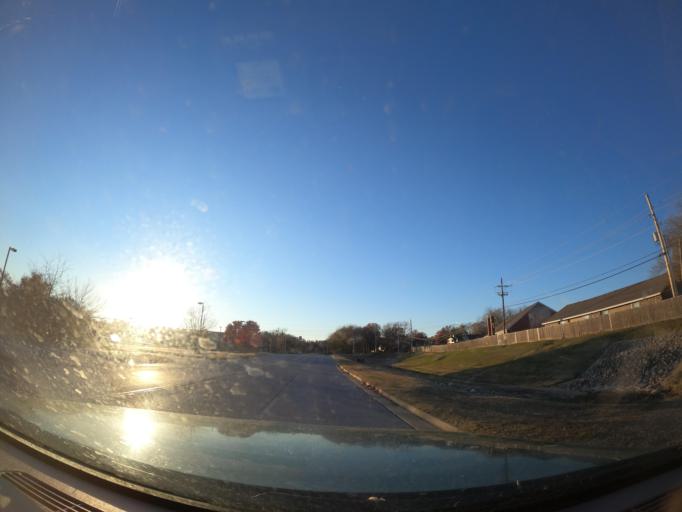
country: US
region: Oklahoma
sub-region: Tulsa County
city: Jenks
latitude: 36.0679
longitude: -95.8850
